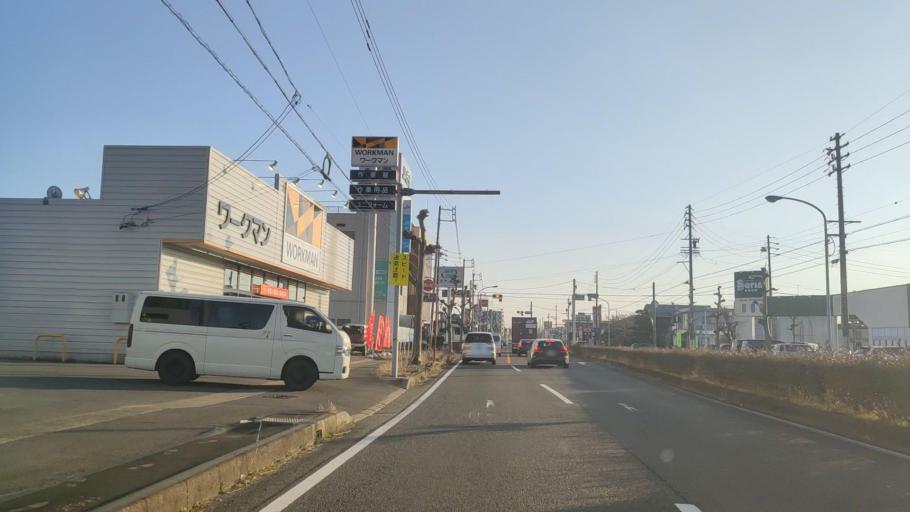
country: JP
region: Gifu
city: Gifu-shi
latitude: 35.4430
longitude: 136.7391
